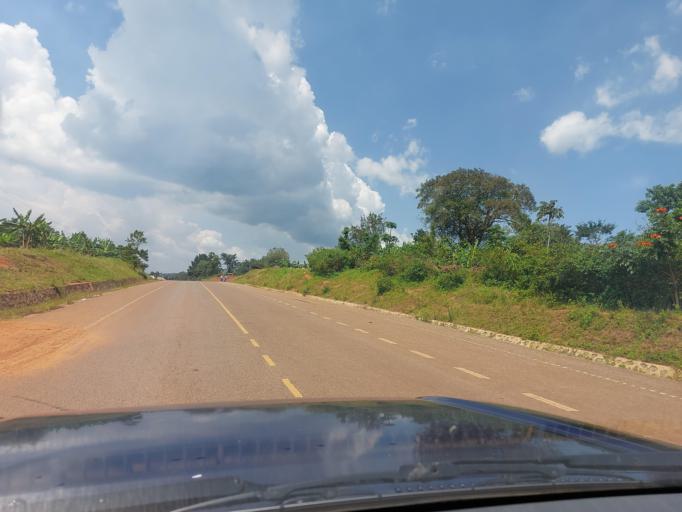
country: UG
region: Central Region
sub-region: Buikwe District
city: Buikwe
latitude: 0.3084
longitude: 33.0990
